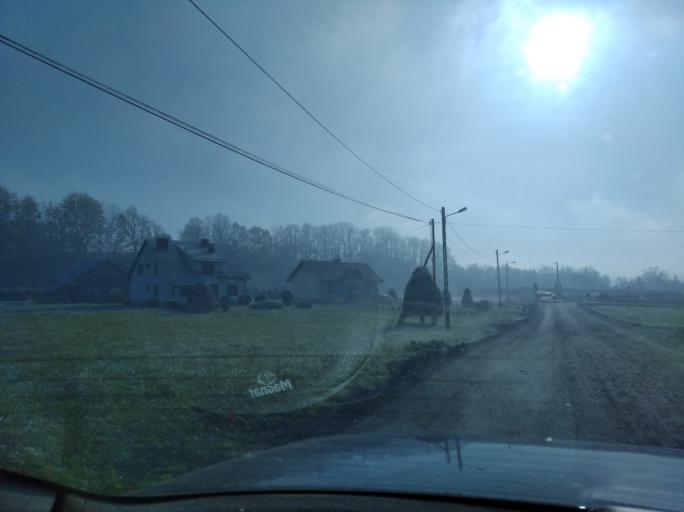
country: PL
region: Subcarpathian Voivodeship
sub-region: Powiat strzyzowski
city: Wysoka Strzyzowska
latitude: 49.8666
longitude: 21.7065
